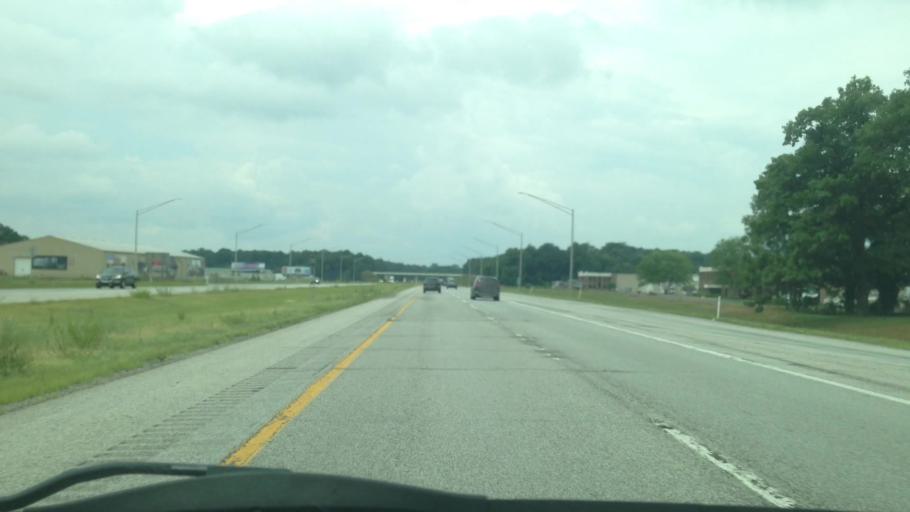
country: US
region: Indiana
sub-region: Elkhart County
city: Bristol
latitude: 41.7351
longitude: -85.7924
